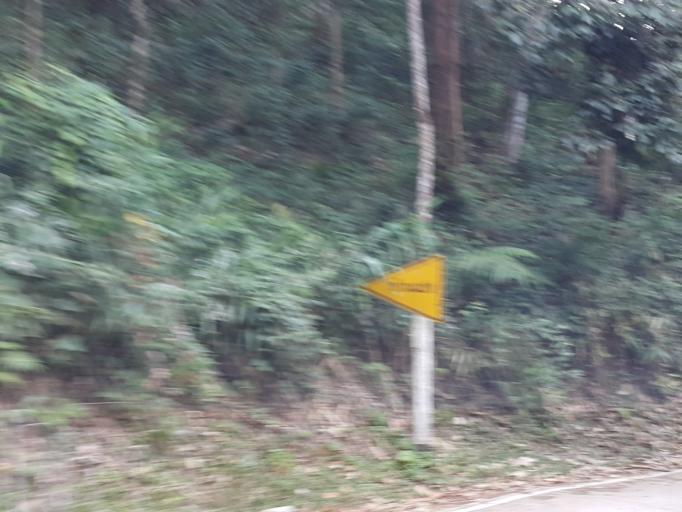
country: TH
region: Chiang Mai
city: Mae On
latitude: 18.8896
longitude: 99.3535
